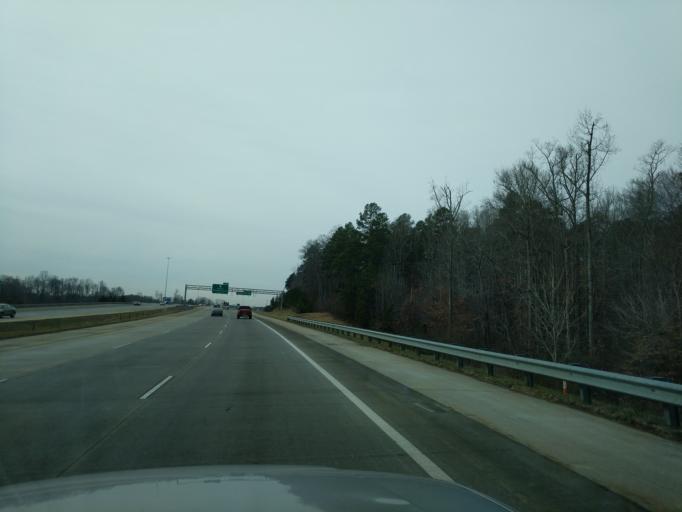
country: US
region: North Carolina
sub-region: Mecklenburg County
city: Huntersville
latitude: 35.3376
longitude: -80.9073
